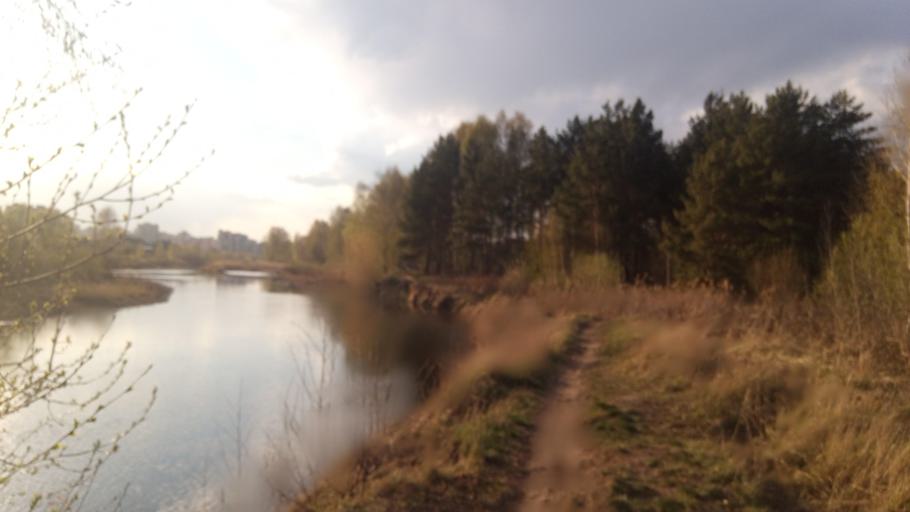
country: RU
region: Chelyabinsk
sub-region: Gorod Chelyabinsk
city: Chelyabinsk
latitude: 55.1565
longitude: 61.3227
